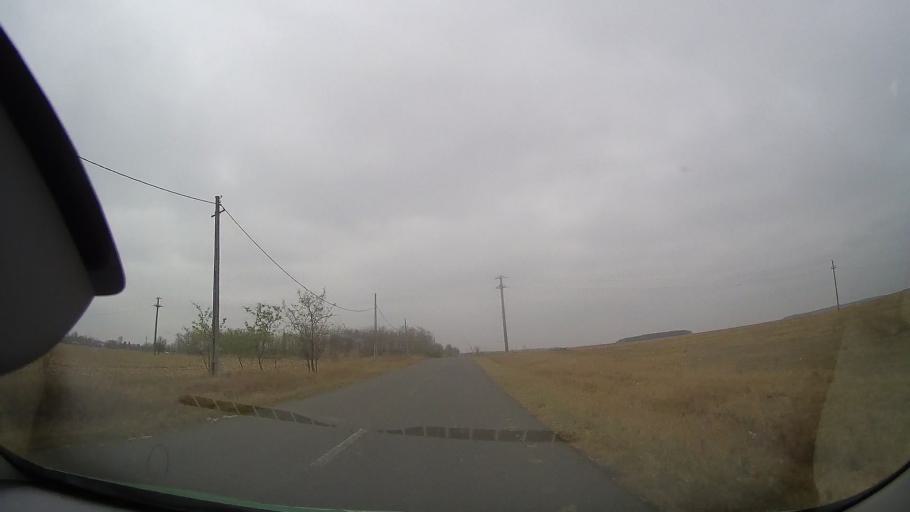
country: RO
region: Buzau
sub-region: Comuna Scutelnici
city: Scutelnici
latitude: 44.8516
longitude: 26.9115
